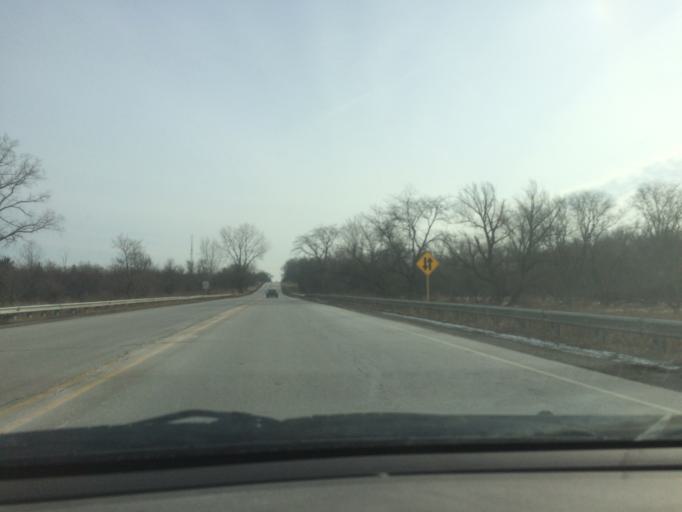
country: US
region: Illinois
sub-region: Cook County
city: Streamwood
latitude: 42.0463
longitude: -88.1752
